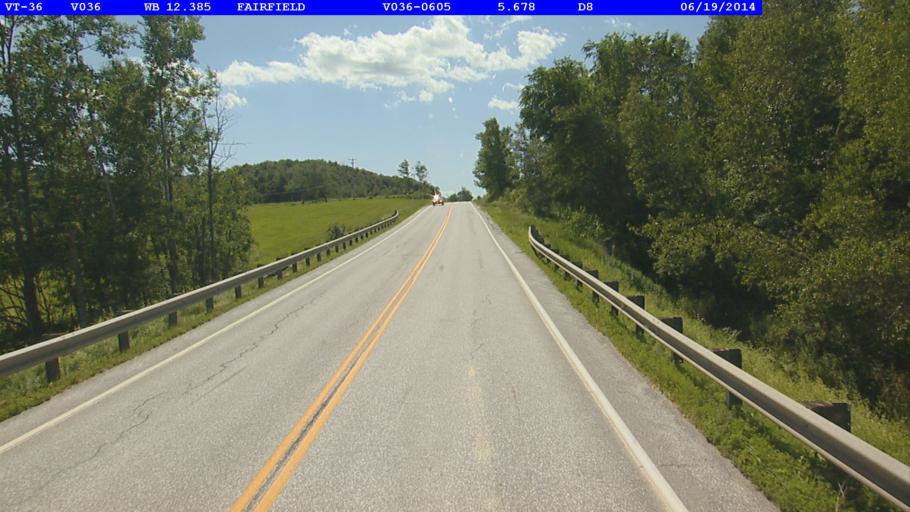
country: US
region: Vermont
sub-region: Franklin County
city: Enosburg Falls
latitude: 44.8046
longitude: -72.9215
